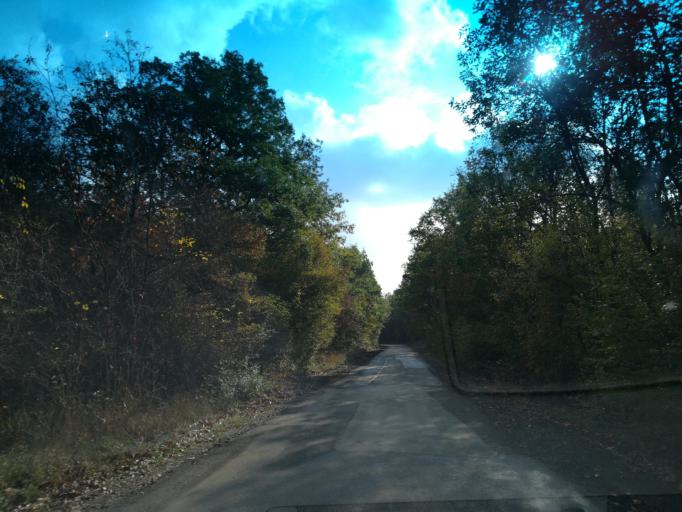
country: BG
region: Stara Zagora
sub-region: Obshtina Nikolaevo
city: Elkhovo
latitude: 42.3229
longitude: 25.3991
